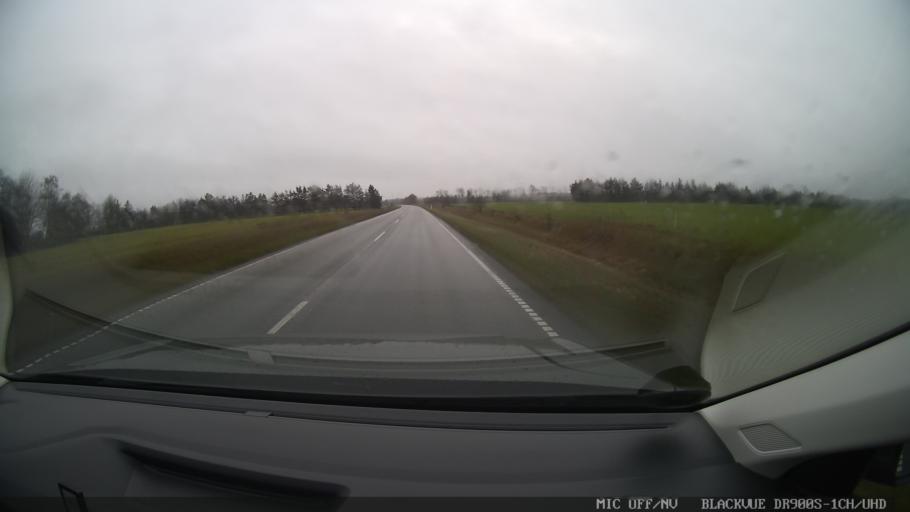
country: DK
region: Central Jutland
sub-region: Herning Kommune
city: Avlum
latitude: 56.2958
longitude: 8.8996
